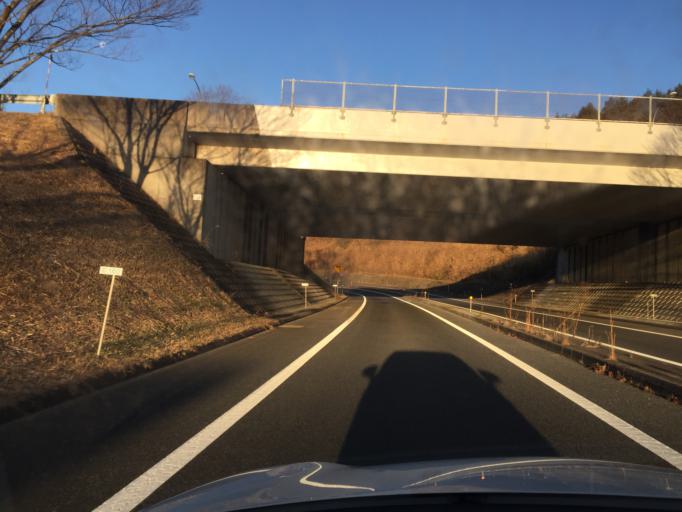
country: JP
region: Ibaraki
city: Kitaibaraki
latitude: 36.7976
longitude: 140.7254
